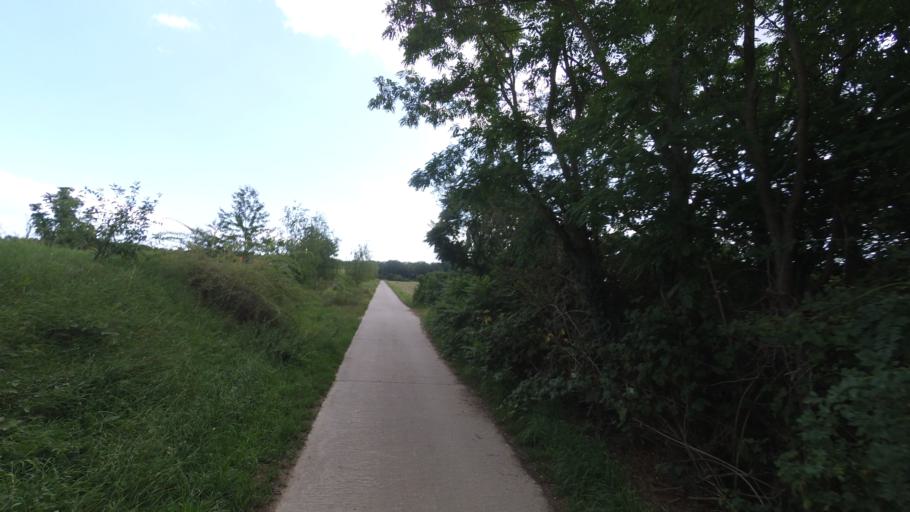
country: DE
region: Rheinland-Pfalz
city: Schifferstadt
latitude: 49.3905
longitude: 8.3984
